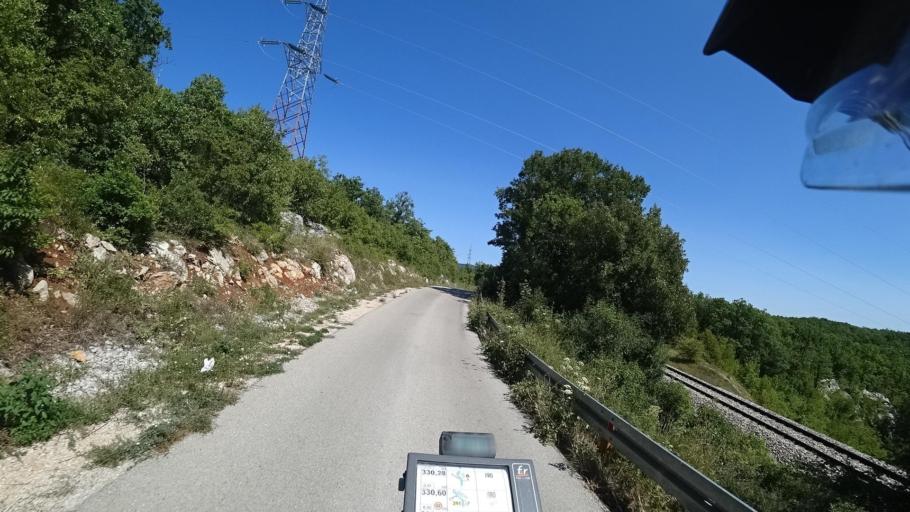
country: HR
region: Licko-Senjska
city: Otocac
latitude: 44.7356
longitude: 15.3612
